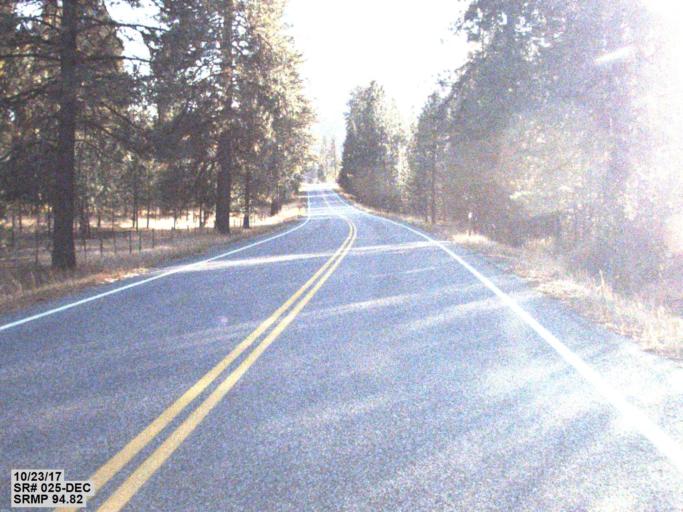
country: US
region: Washington
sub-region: Stevens County
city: Kettle Falls
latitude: 48.7580
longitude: -118.0397
